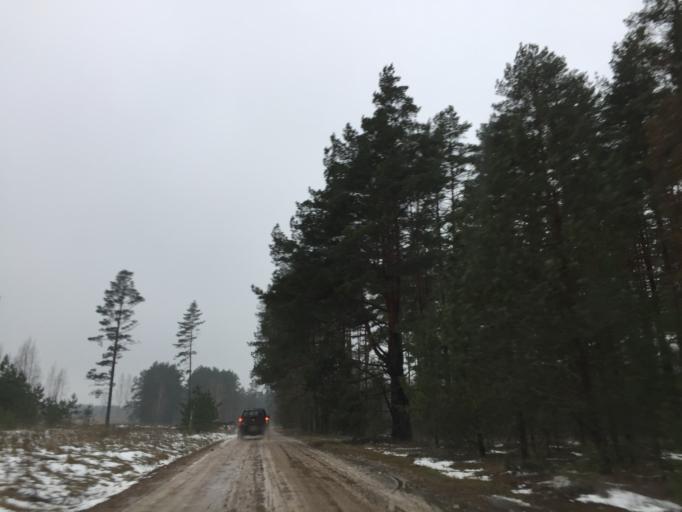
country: LV
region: Incukalns
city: Vangazi
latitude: 57.1307
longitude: 24.5799
